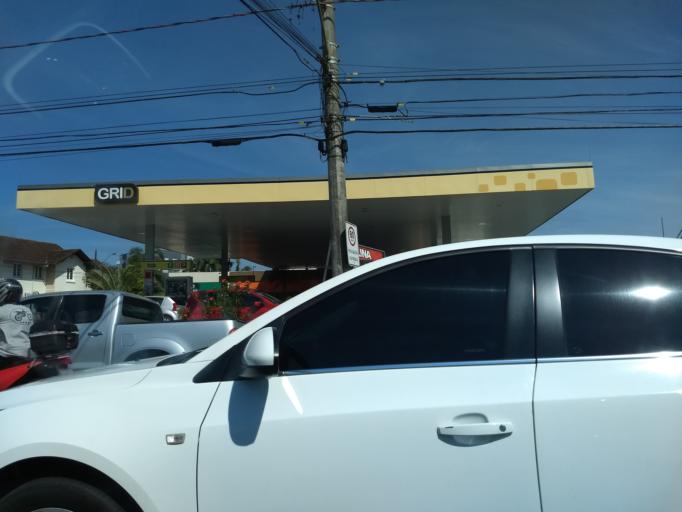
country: BR
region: Santa Catarina
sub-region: Jaragua Do Sul
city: Jaragua do Sul
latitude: -26.4942
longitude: -49.0870
